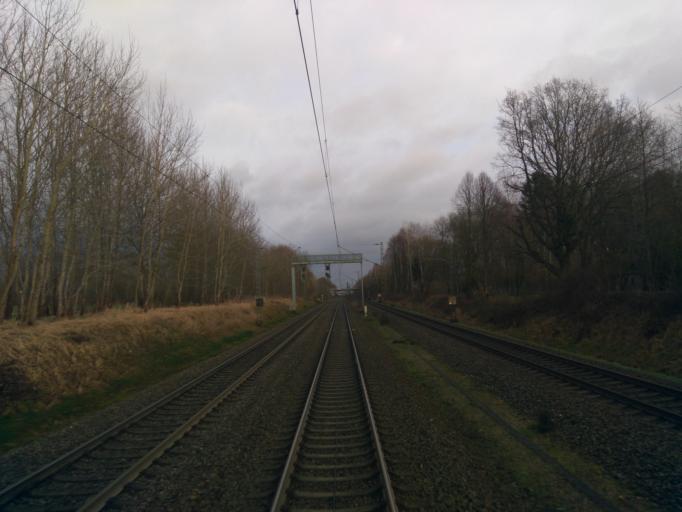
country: DE
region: Lower Saxony
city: Tostedt
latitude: 53.2660
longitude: 9.7189
